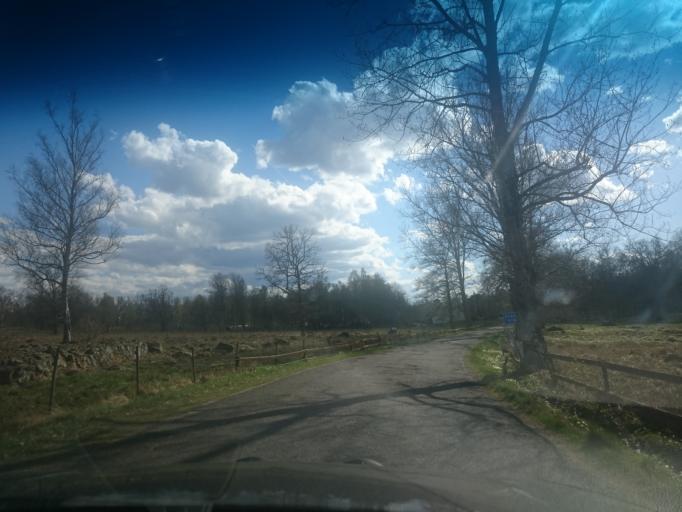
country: SE
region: Kronoberg
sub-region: Vaxjo Kommun
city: Braas
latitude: 57.1408
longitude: 15.1496
